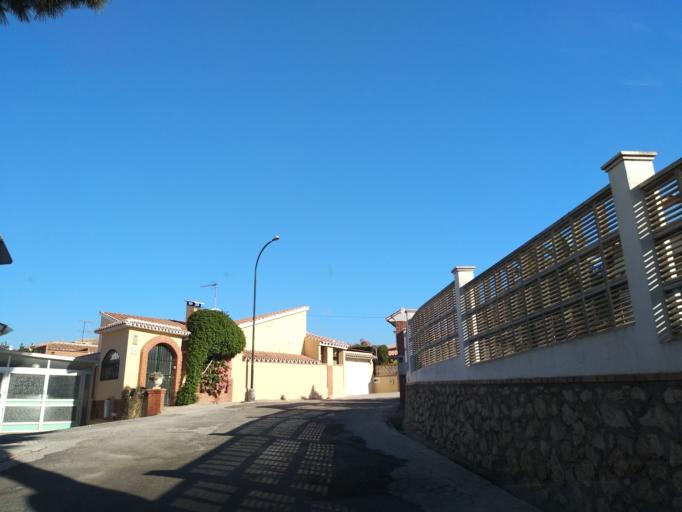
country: ES
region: Andalusia
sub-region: Provincia de Malaga
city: Valdes
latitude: 36.7169
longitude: -4.1928
